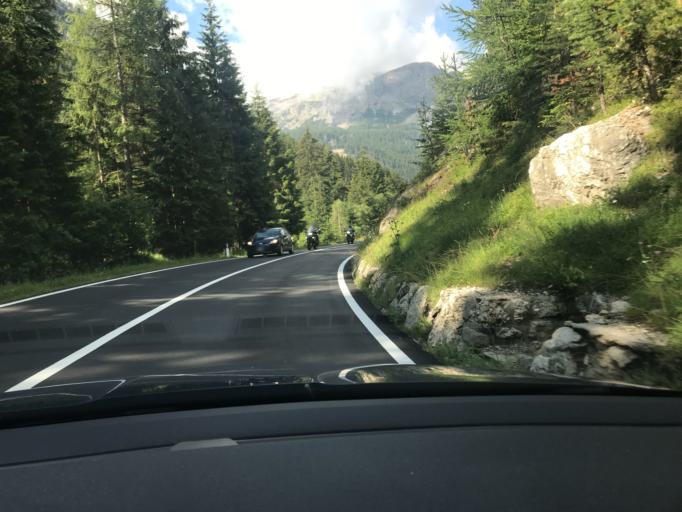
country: IT
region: Trentino-Alto Adige
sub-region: Bolzano
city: Corvara in Badia
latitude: 46.5601
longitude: 11.8820
